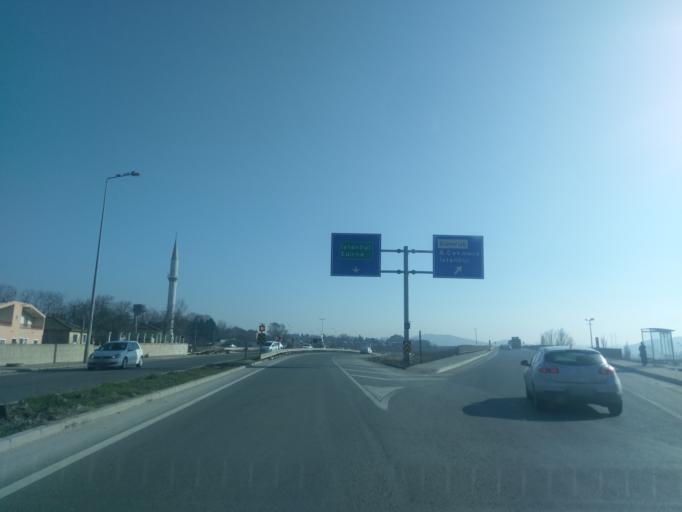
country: TR
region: Istanbul
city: Muratbey
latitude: 41.0893
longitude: 28.5142
